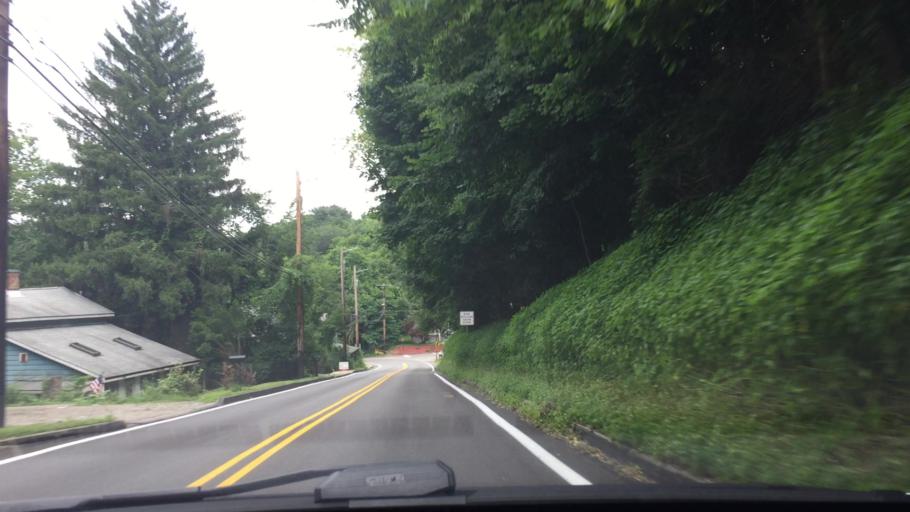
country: US
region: Pennsylvania
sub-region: Allegheny County
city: Rennerdale
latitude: 40.3789
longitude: -80.1499
